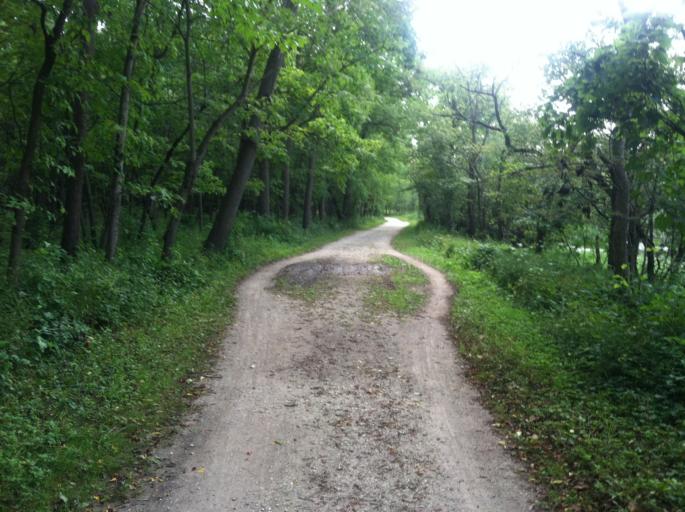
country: US
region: Illinois
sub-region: Lake County
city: Riverwoods
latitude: 42.1479
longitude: -87.9072
